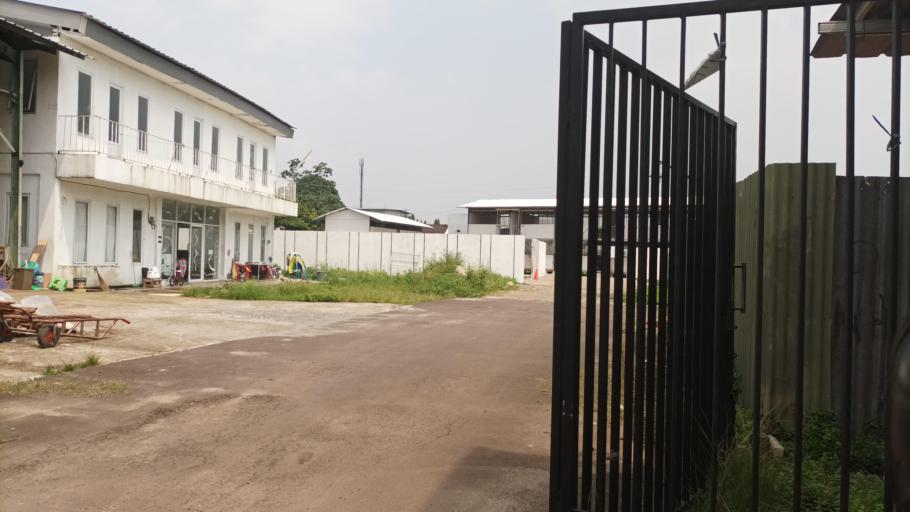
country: ID
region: West Java
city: Depok
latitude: -6.3729
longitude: 106.8594
